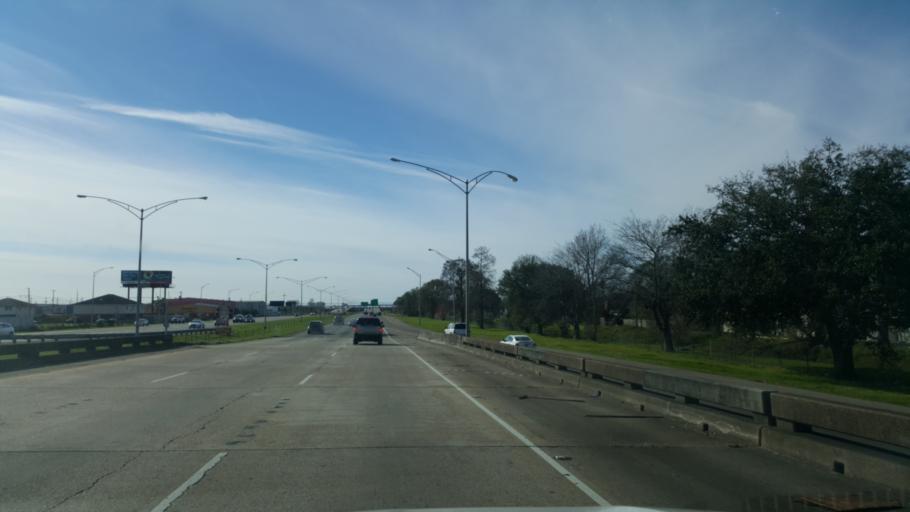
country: US
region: Louisiana
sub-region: Jefferson Parish
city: Kenner
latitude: 30.0083
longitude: -90.2693
